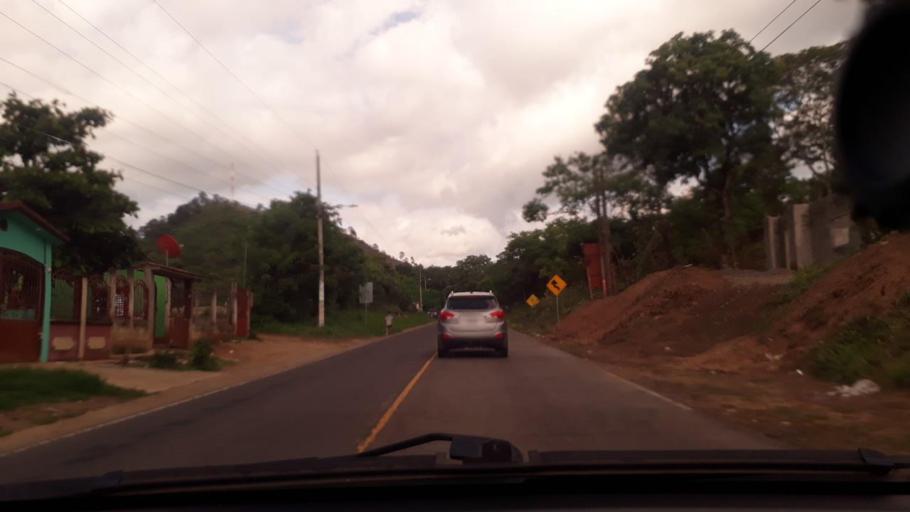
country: GT
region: Jutiapa
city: Quesada
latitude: 14.2744
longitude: -89.9989
